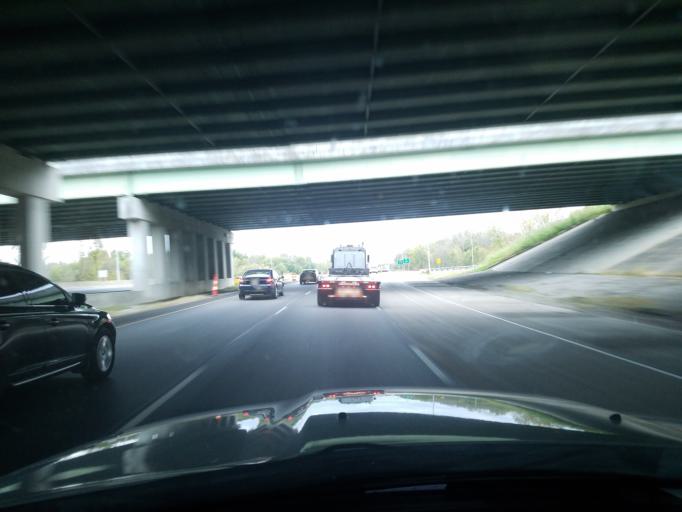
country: US
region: Indiana
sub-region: Vanderburgh County
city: Evansville
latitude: 37.9403
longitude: -87.5438
